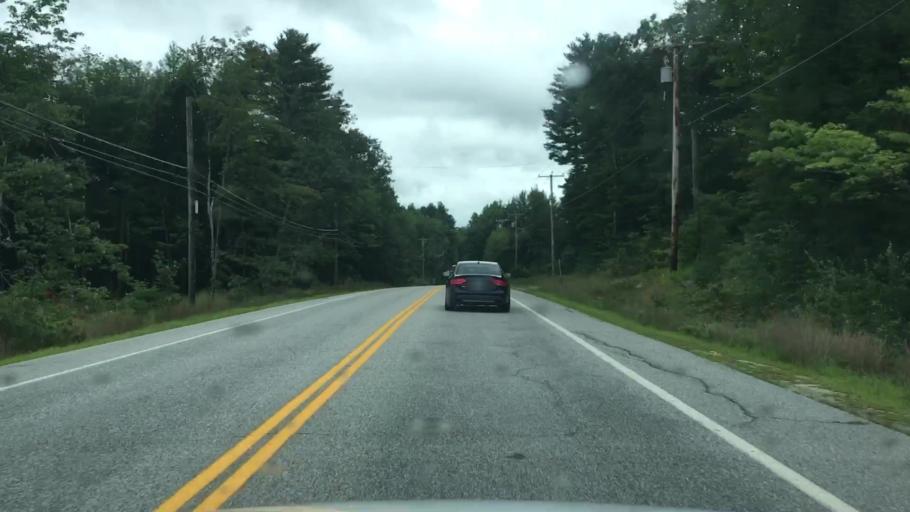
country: US
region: Maine
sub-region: York County
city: Cornish
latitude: 43.8380
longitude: -70.7799
